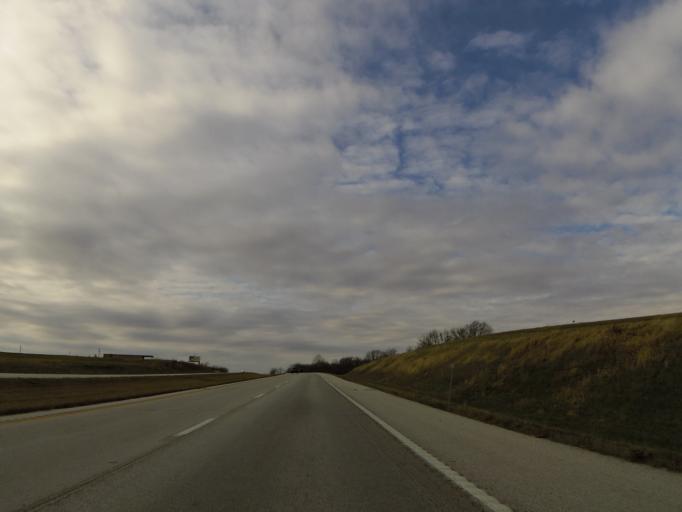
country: US
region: Missouri
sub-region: Marion County
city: Hannibal
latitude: 39.7409
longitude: -91.4188
